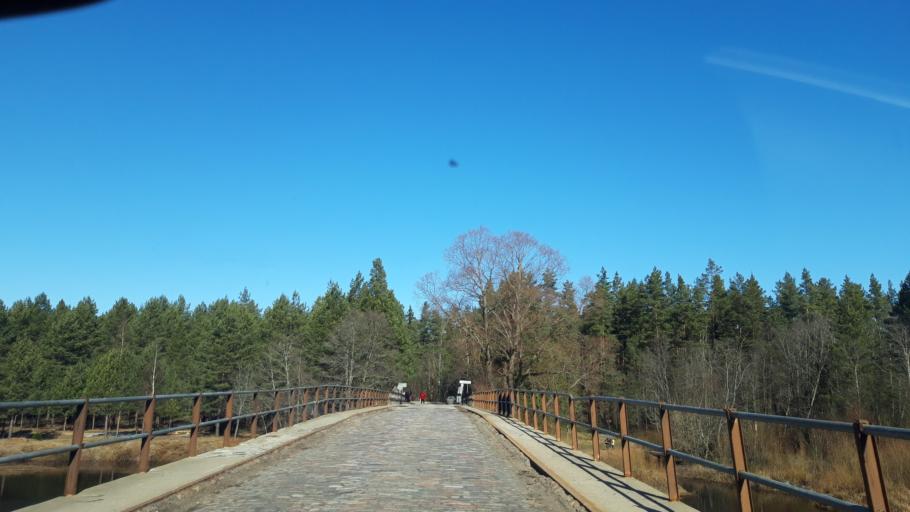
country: LV
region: Strenci
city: Strenci
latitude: 57.6183
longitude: 25.7014
